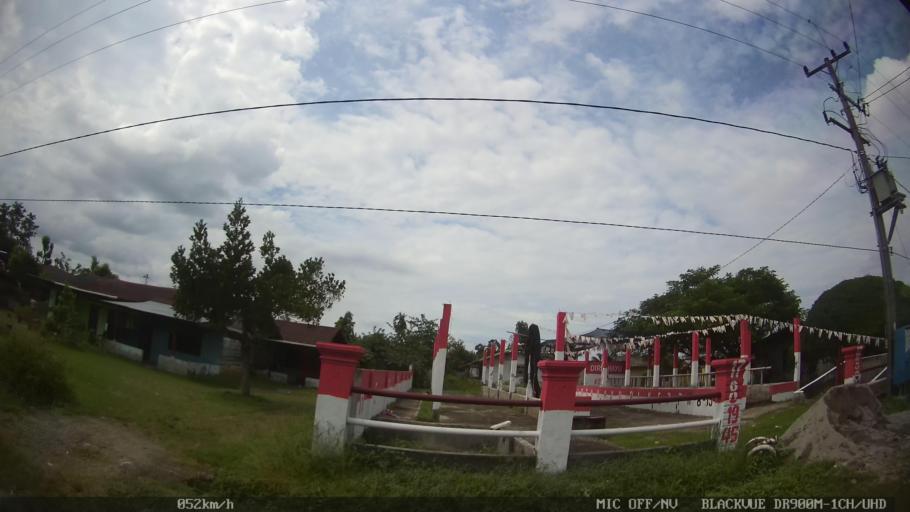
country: ID
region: North Sumatra
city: Sunggal
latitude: 3.6359
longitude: 98.5968
